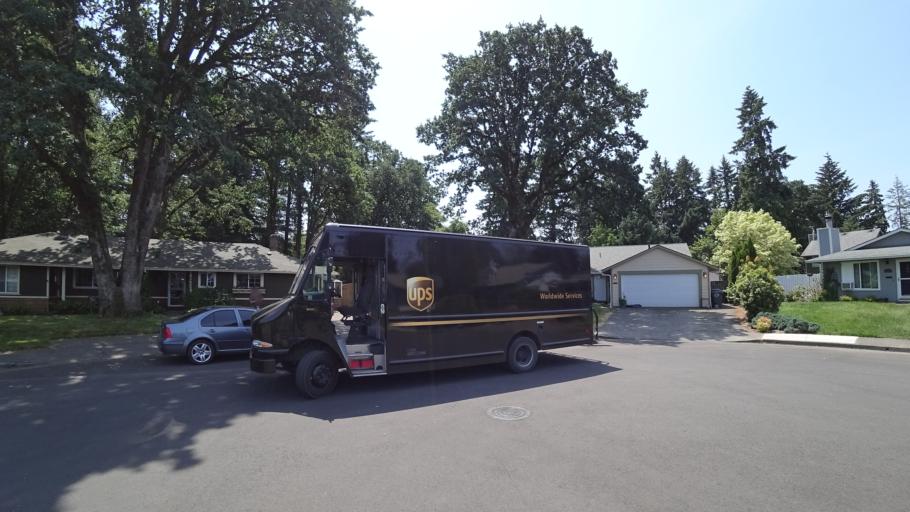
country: US
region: Oregon
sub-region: Washington County
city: Hillsboro
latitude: 45.4981
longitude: -122.9359
